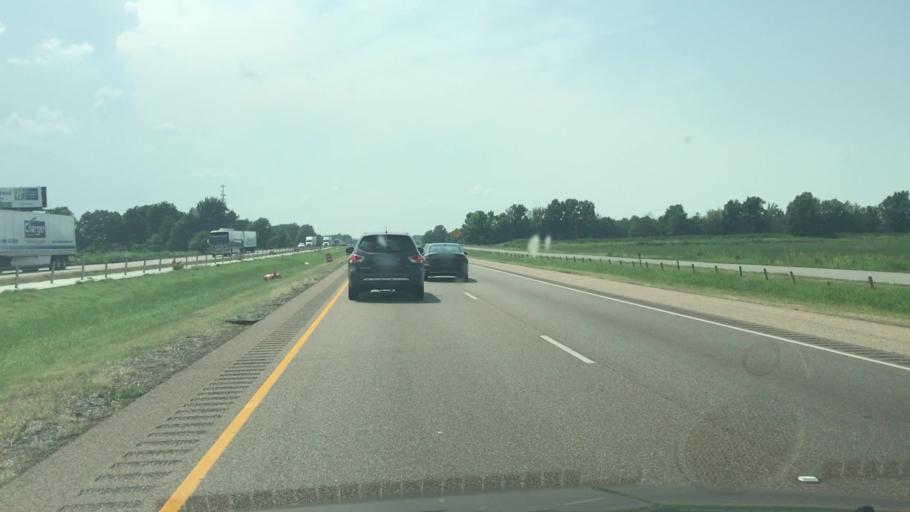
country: US
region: Arkansas
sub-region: Crittenden County
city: West Memphis
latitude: 35.1494
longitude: -90.3515
